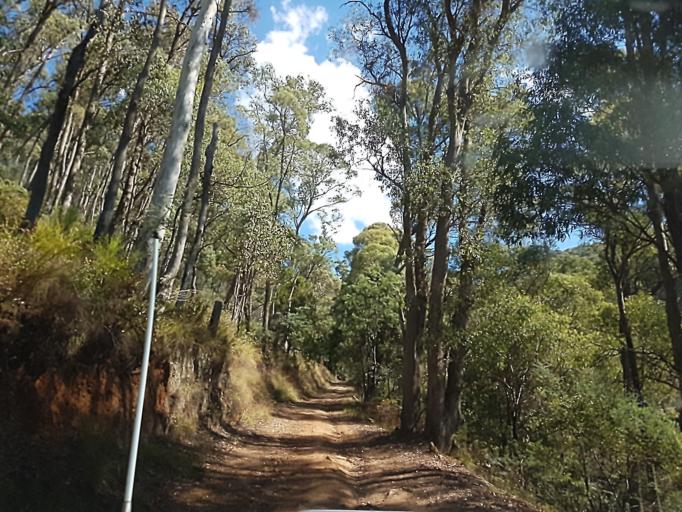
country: AU
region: Victoria
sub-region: Alpine
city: Mount Beauty
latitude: -36.8791
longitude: 147.0442
